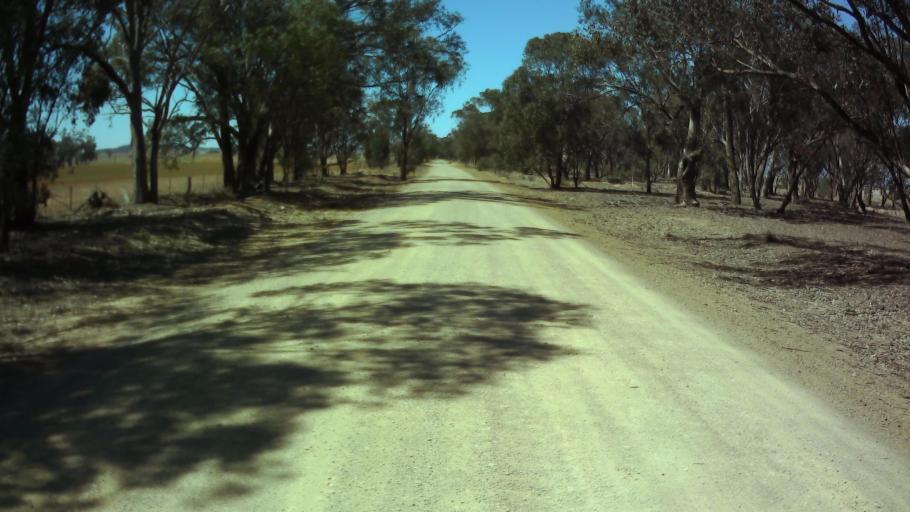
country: AU
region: New South Wales
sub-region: Weddin
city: Grenfell
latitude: -33.8708
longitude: 148.0886
